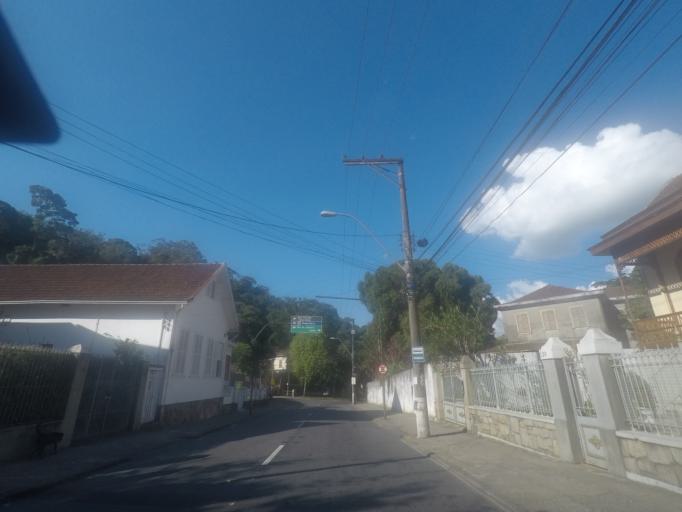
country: BR
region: Rio de Janeiro
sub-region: Petropolis
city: Petropolis
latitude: -22.5131
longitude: -43.1725
